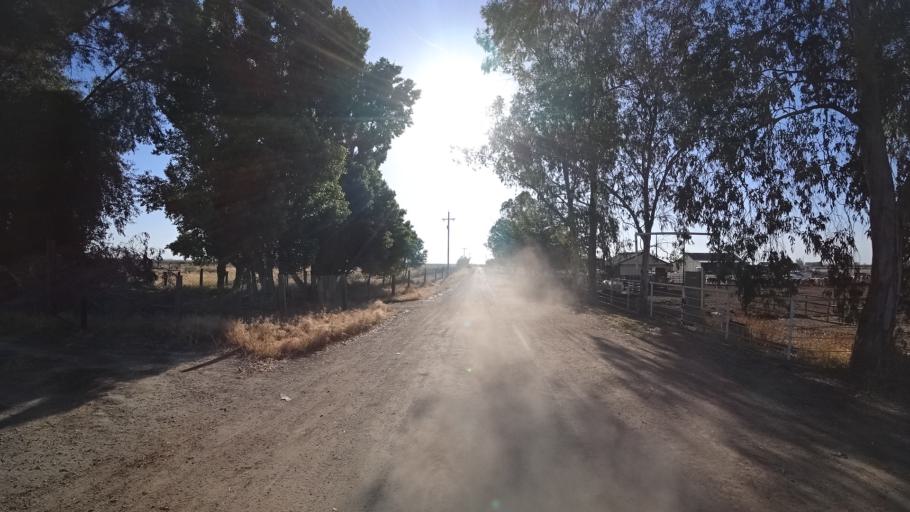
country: US
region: California
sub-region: Kings County
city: Stratford
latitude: 36.1748
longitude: -119.7834
